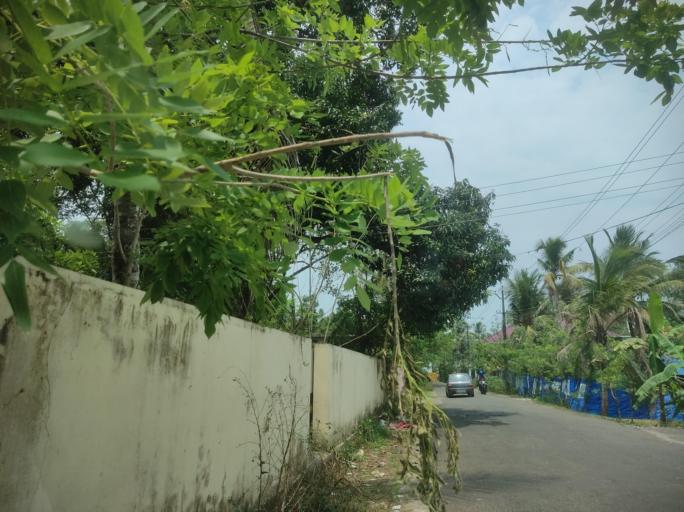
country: IN
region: Kerala
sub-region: Alappuzha
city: Kutiatodu
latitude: 9.7507
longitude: 76.3253
